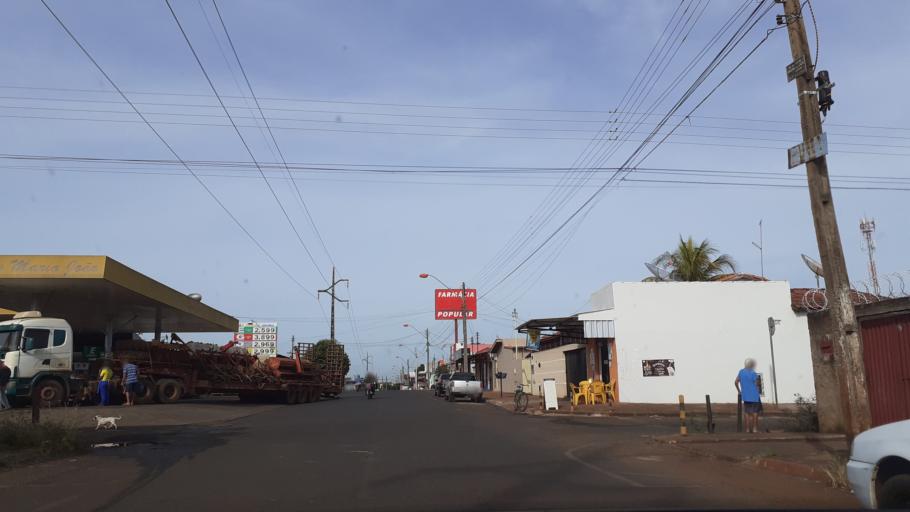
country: BR
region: Goias
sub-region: Itumbiara
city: Itumbiara
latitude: -18.4158
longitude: -49.2443
